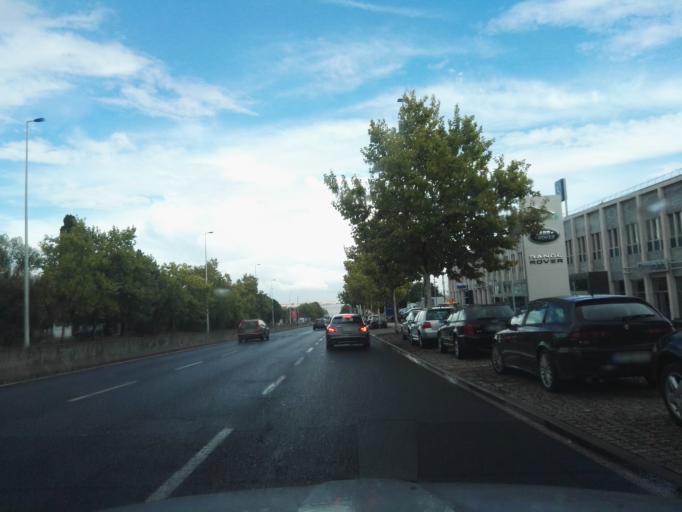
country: PT
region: Lisbon
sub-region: Loures
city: Moscavide
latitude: 38.7594
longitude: -9.1151
